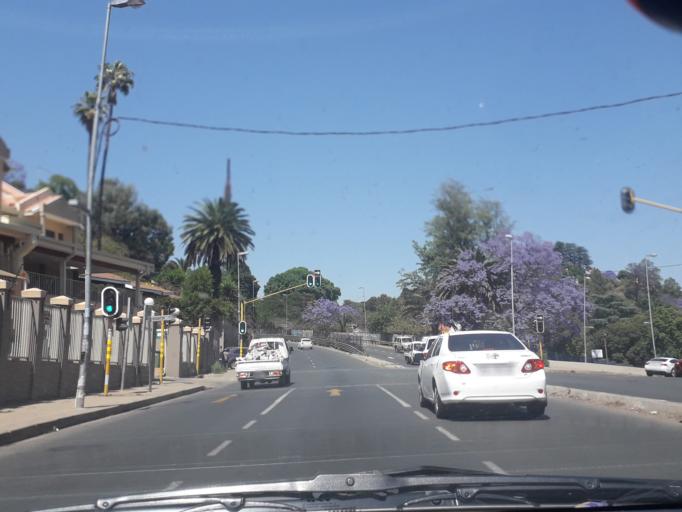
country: ZA
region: Gauteng
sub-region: City of Johannesburg Metropolitan Municipality
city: Johannesburg
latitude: -26.1695
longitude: 28.0747
